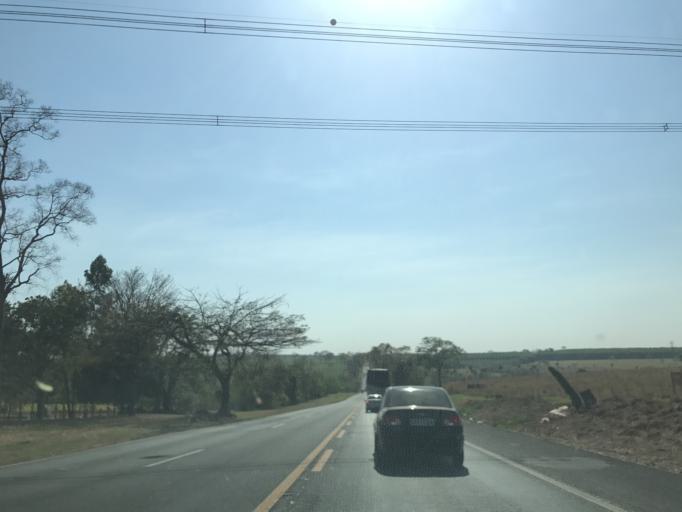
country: BR
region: Sao Paulo
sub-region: Bady Bassitt
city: Bady Bassitt
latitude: -20.9531
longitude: -49.5497
